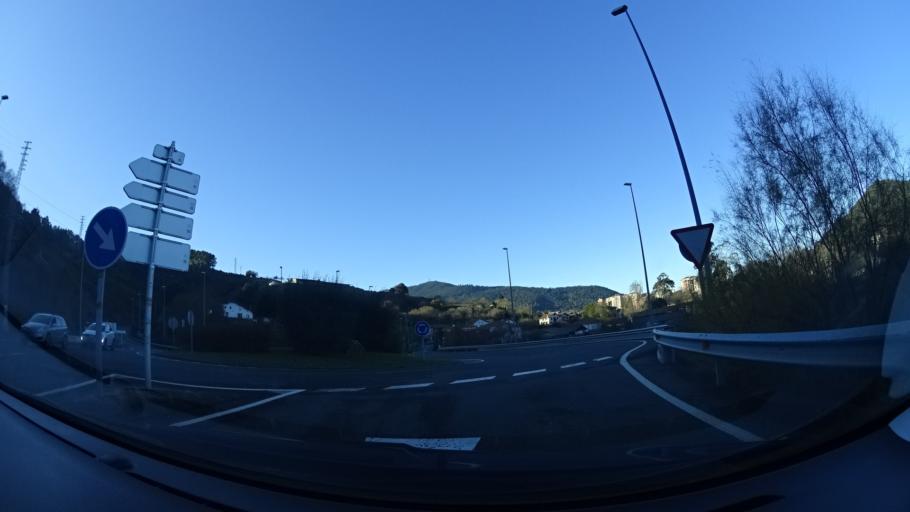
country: ES
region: Basque Country
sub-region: Bizkaia
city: Lekeitio
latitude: 43.3550
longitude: -2.5040
